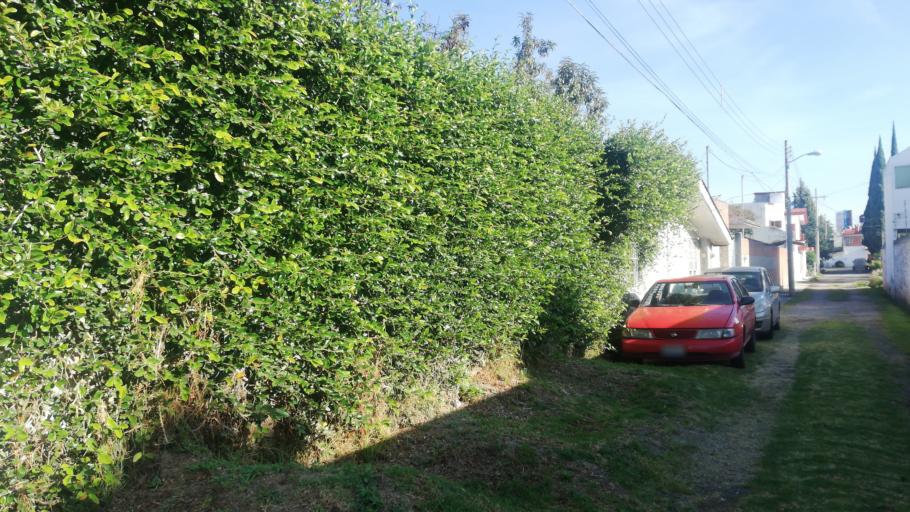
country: MX
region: Puebla
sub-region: San Pedro Cholula
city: Santiago Momoxpan
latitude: 19.0569
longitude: -98.2726
